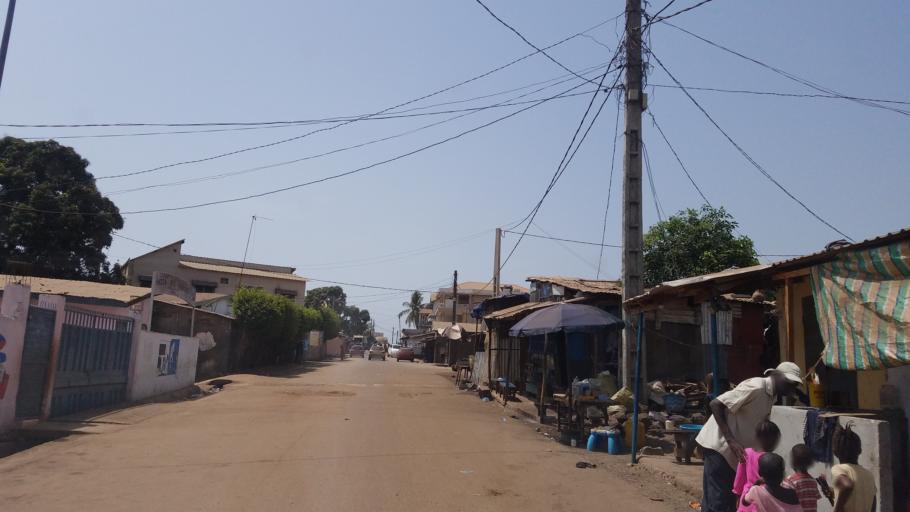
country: GN
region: Conakry
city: Conakry
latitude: 9.5769
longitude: -13.6597
